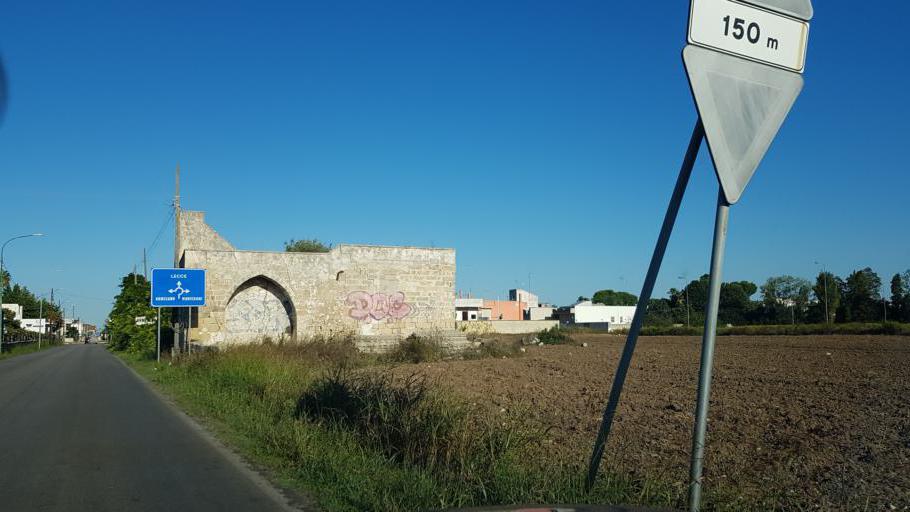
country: IT
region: Apulia
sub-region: Provincia di Lecce
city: Arnesano
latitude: 40.3312
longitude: 18.0903
